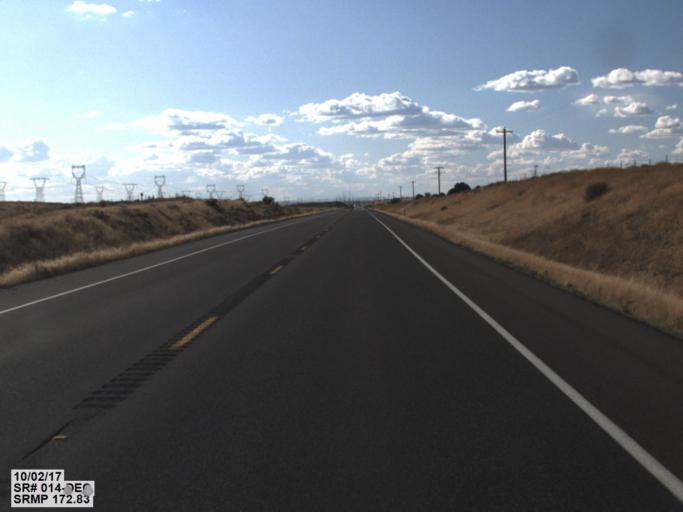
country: US
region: Oregon
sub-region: Morrow County
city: Irrigon
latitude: 45.9455
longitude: -119.4882
